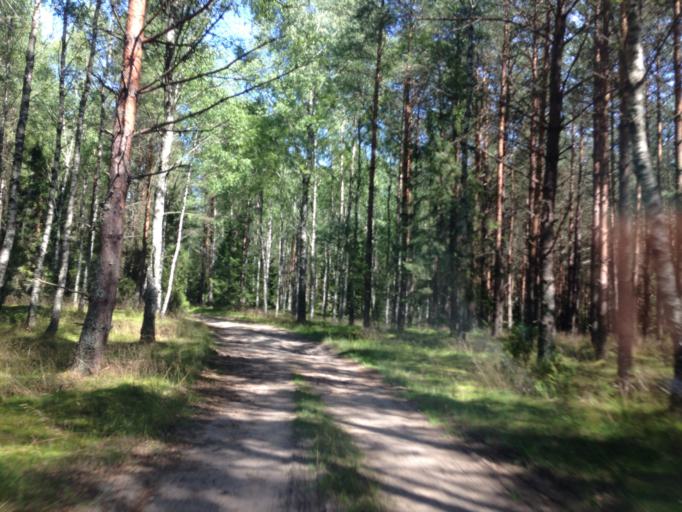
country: PL
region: Pomeranian Voivodeship
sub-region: Powiat koscierski
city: Dziemiany
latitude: 53.9865
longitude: 17.8342
